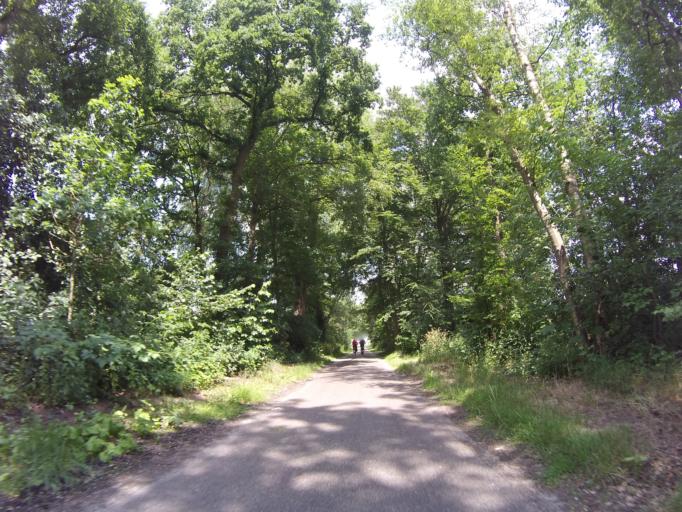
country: NL
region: Utrecht
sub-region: Gemeente De Bilt
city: De Bilt
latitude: 52.1387
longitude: 5.1639
